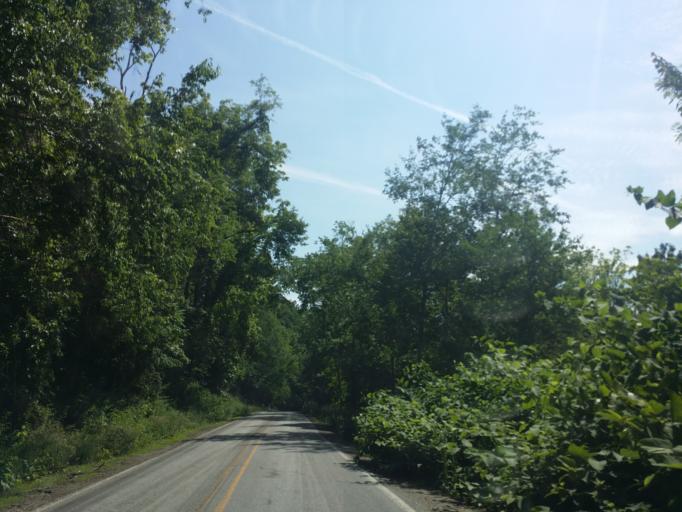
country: US
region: North Carolina
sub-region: Haywood County
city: Cove Creek
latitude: 35.7722
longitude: -82.8971
